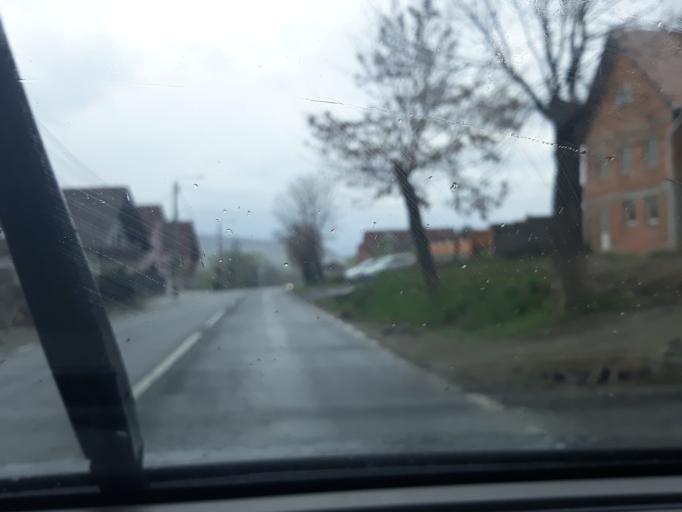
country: RO
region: Harghita
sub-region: Comuna Corund
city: Corund
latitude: 46.4786
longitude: 25.1744
